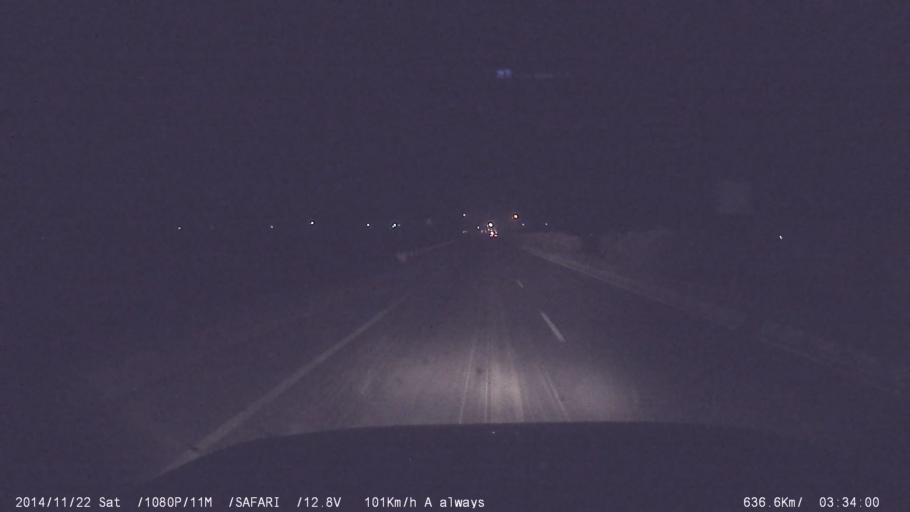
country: IN
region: Tamil Nadu
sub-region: Salem
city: Konganapuram
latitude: 11.4922
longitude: 77.8934
